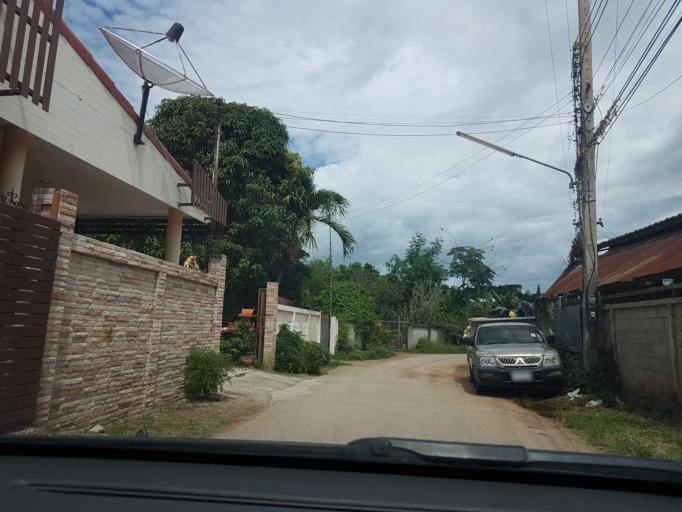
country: TH
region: Lampang
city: Ko Kha
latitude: 18.2223
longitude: 99.4156
